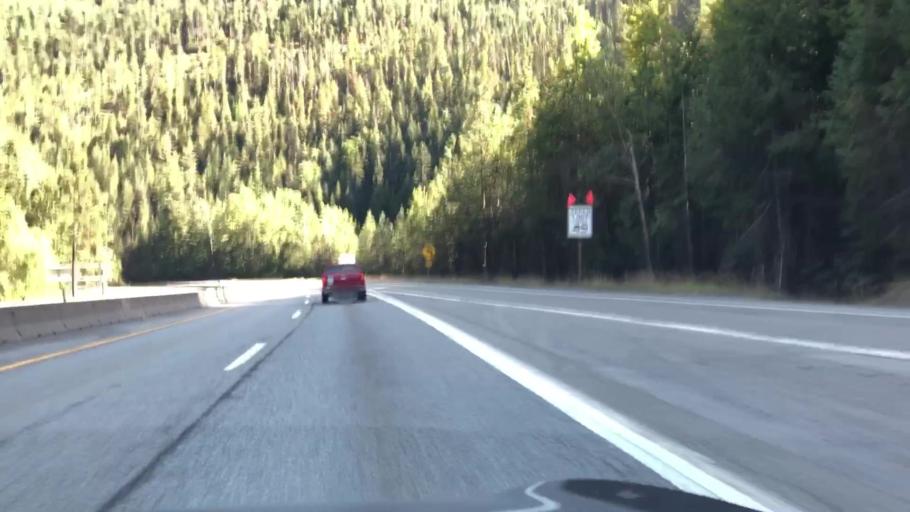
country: US
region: Idaho
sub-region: Shoshone County
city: Wallace
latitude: 47.4642
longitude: -115.8100
